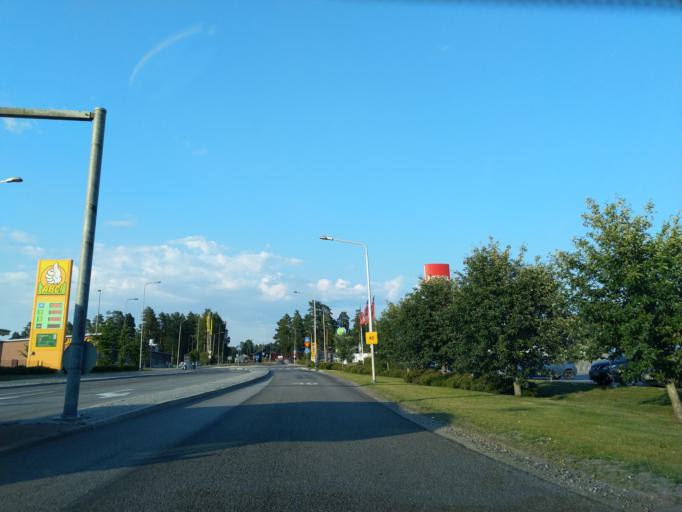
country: FI
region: Satakunta
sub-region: Pohjois-Satakunta
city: Kankaanpaeae
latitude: 61.8127
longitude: 22.3755
